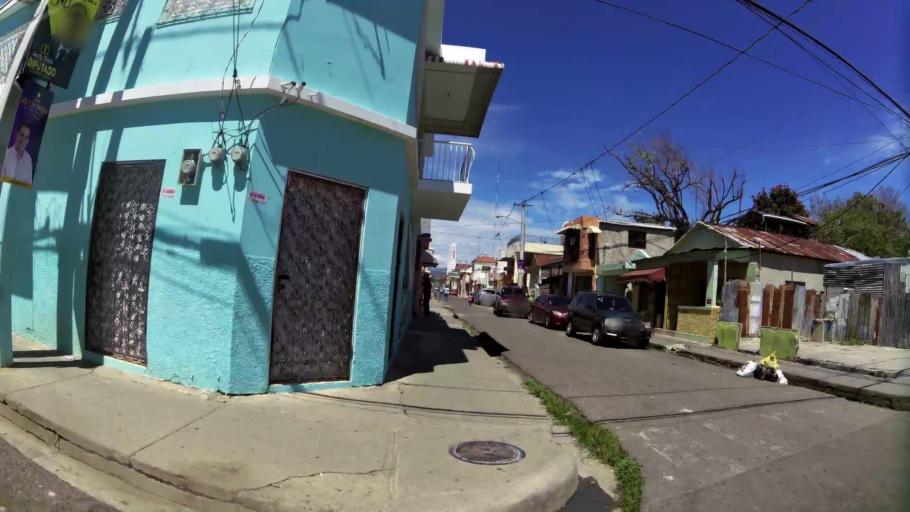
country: DO
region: Santiago
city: Santiago de los Caballeros
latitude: 19.4472
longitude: -70.7000
